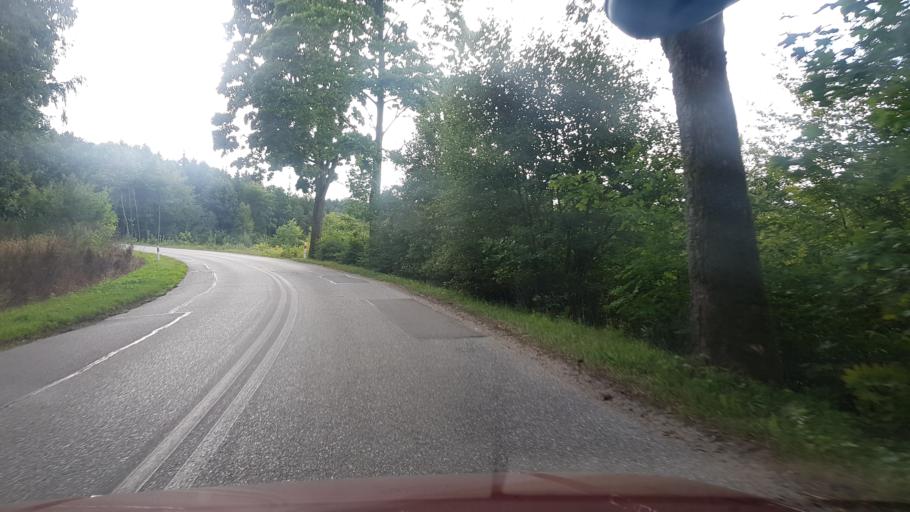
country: PL
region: West Pomeranian Voivodeship
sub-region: Powiat koszalinski
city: Polanow
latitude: 54.0896
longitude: 16.8350
